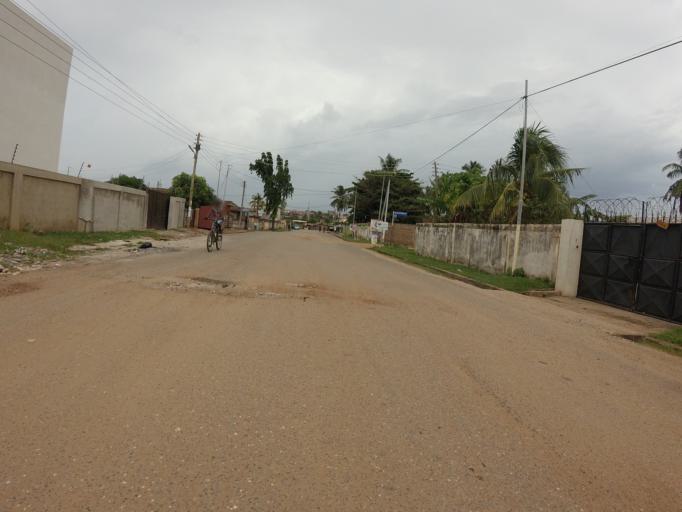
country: GH
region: Greater Accra
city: Accra
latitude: 5.6037
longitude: -0.2098
